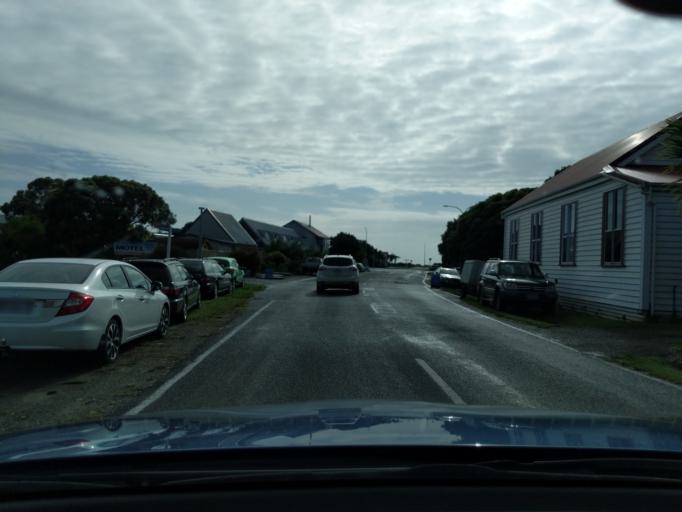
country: NZ
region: Tasman
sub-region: Tasman District
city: Takaka
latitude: -40.6778
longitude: 172.6815
